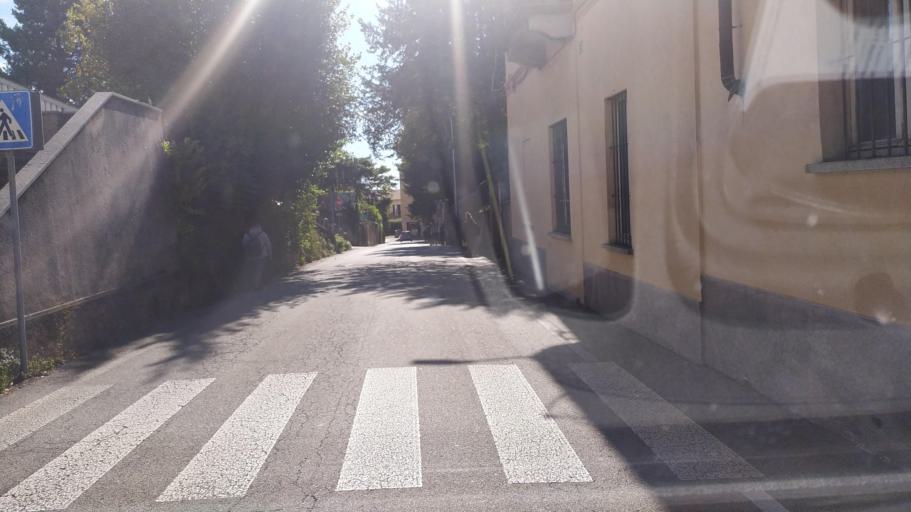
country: IT
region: Lombardy
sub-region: Provincia di Varese
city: Varese
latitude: 45.8165
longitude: 8.8137
